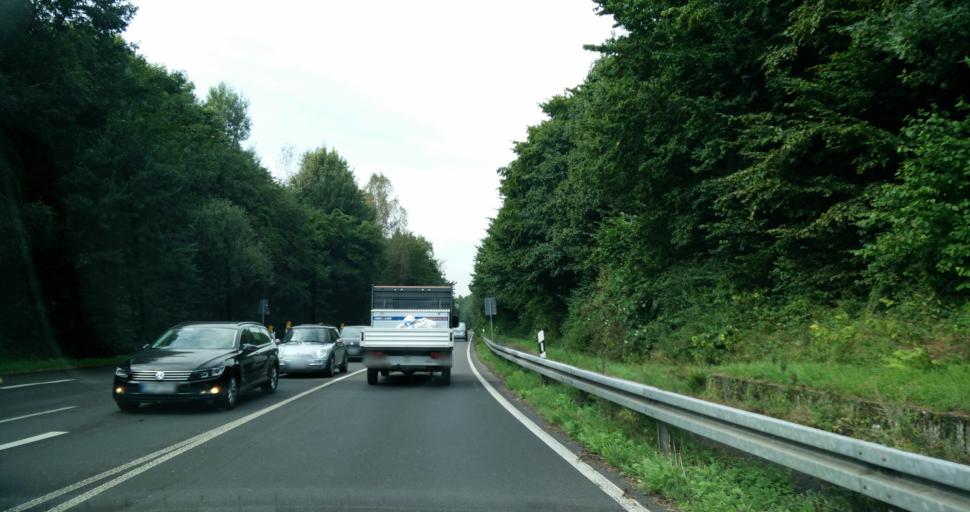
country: DE
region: North Rhine-Westphalia
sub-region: Regierungsbezirk Dusseldorf
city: Mettmann
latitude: 51.2562
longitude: 6.9494
